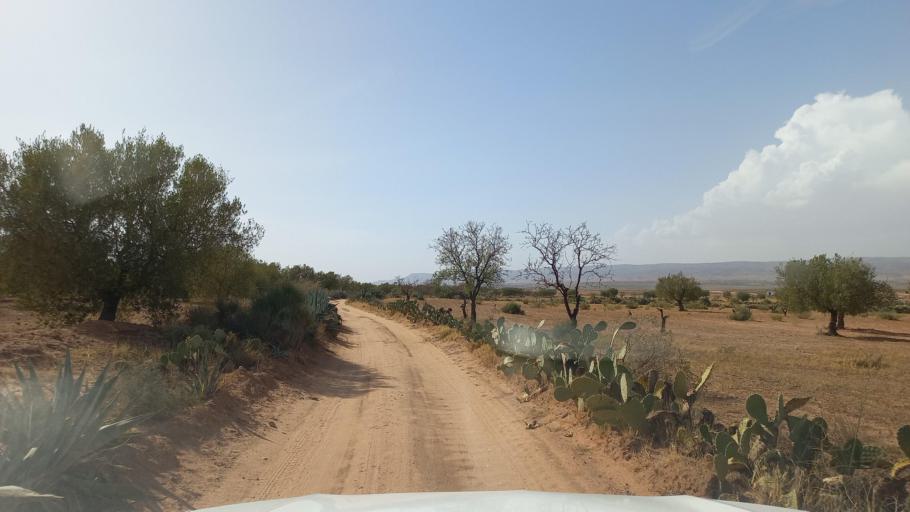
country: TN
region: Al Qasrayn
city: Kasserine
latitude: 35.2108
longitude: 8.9804
